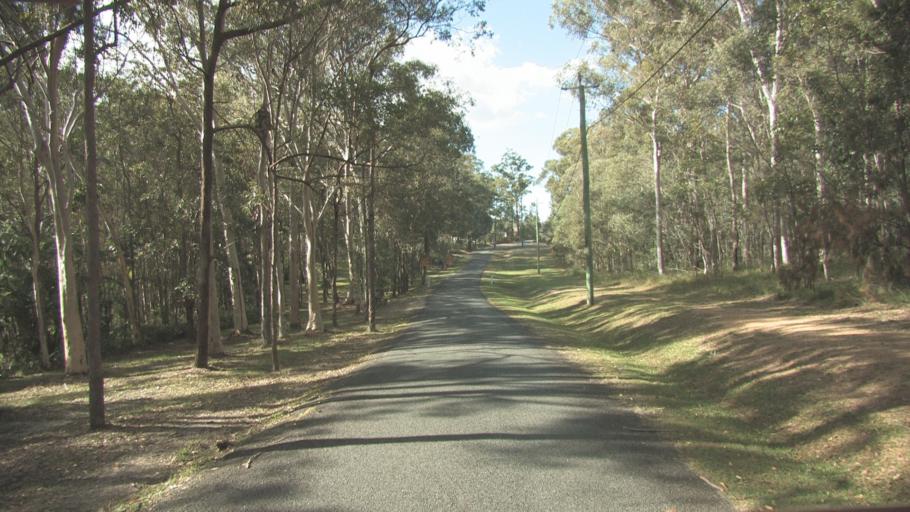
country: AU
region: Queensland
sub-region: Redland
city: Redland Bay
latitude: -27.6522
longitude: 153.2534
